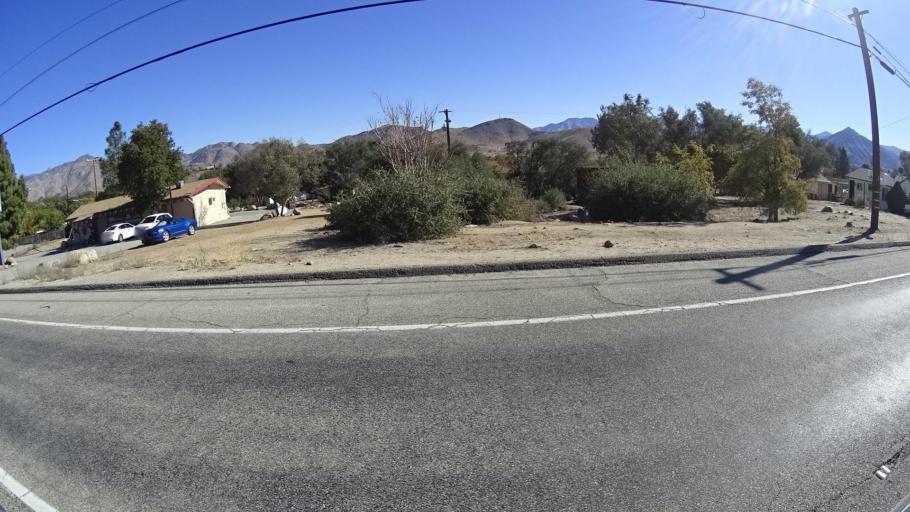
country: US
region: California
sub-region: Kern County
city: Wofford Heights
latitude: 35.7065
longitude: -118.4566
